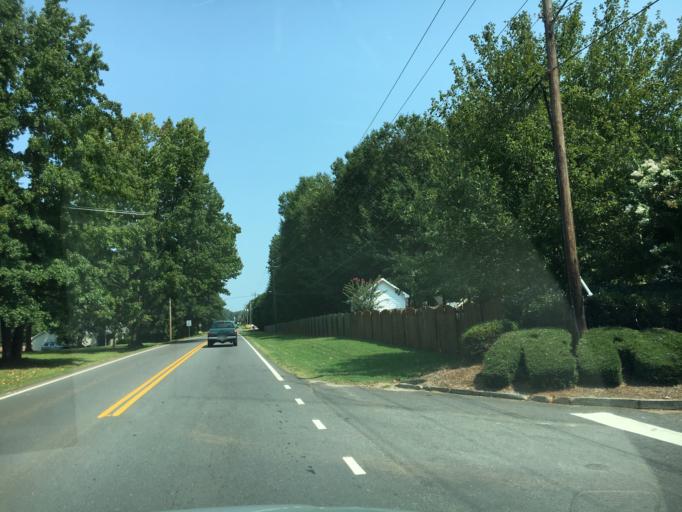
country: US
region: South Carolina
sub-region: Spartanburg County
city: Valley Falls
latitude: 35.0315
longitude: -81.9488
